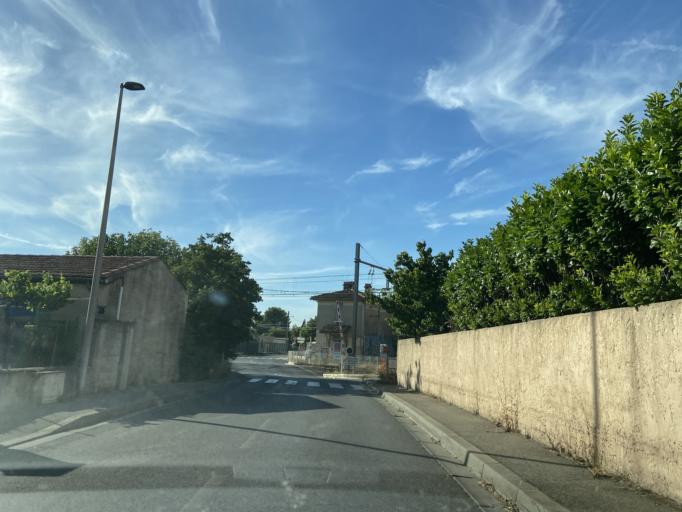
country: FR
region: Provence-Alpes-Cote d'Azur
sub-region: Departement des Bouches-du-Rhone
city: Miramas
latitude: 43.5808
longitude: 5.0072
